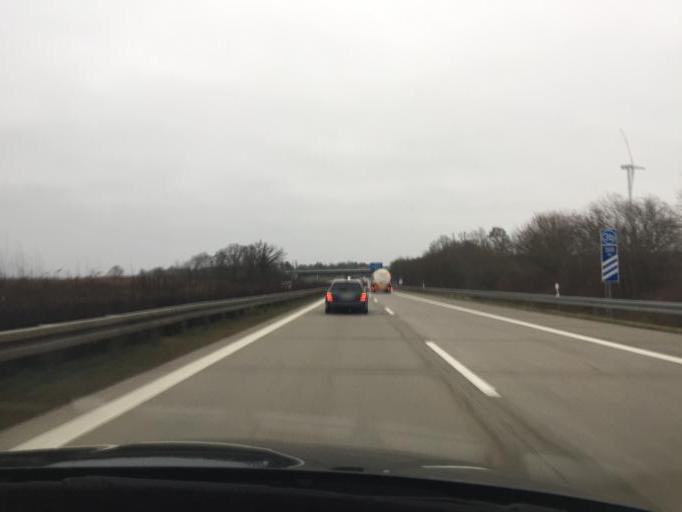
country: DE
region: Brandenburg
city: Mittenwalde
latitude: 52.2490
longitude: 13.5872
